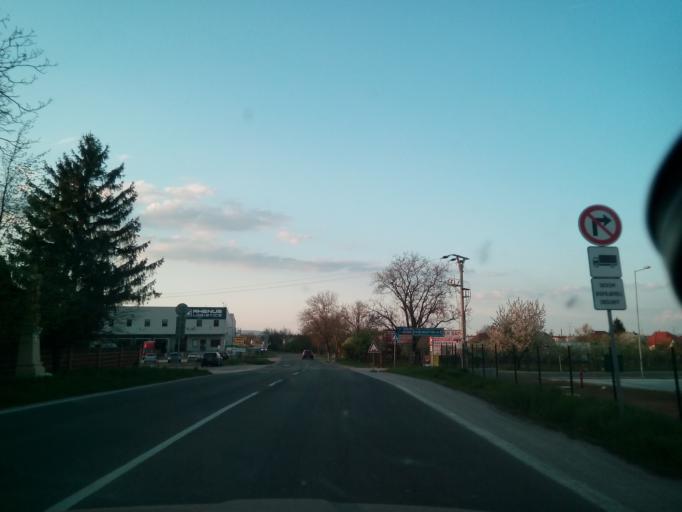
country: SK
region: Trnavsky
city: Vrbove
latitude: 48.5936
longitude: 17.7479
